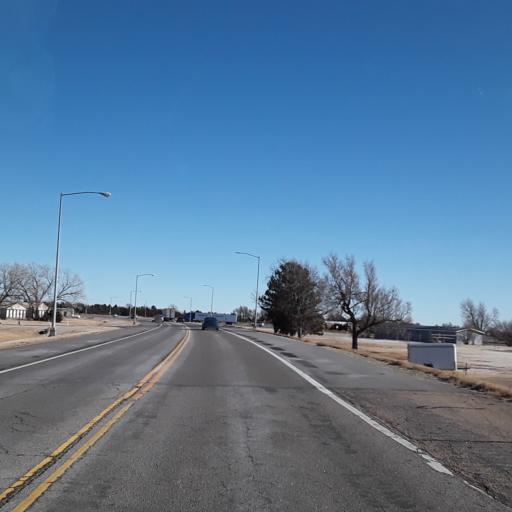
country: US
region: Kansas
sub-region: Pawnee County
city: Larned
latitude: 38.1886
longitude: -99.0865
